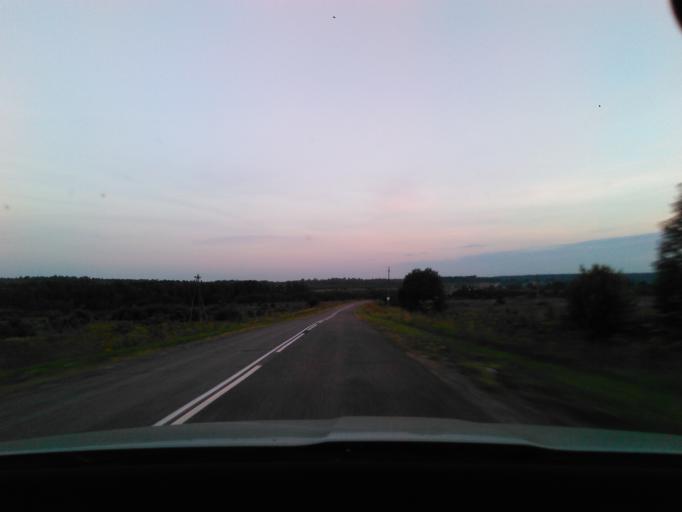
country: RU
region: Moskovskaya
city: Klin
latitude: 56.2292
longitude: 36.7464
